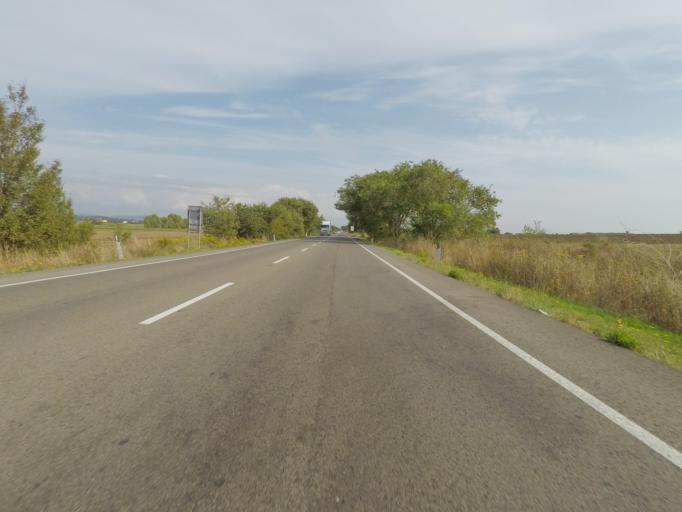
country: IT
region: Tuscany
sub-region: Provincia di Grosseto
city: Capalbio
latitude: 42.4149
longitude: 11.3930
